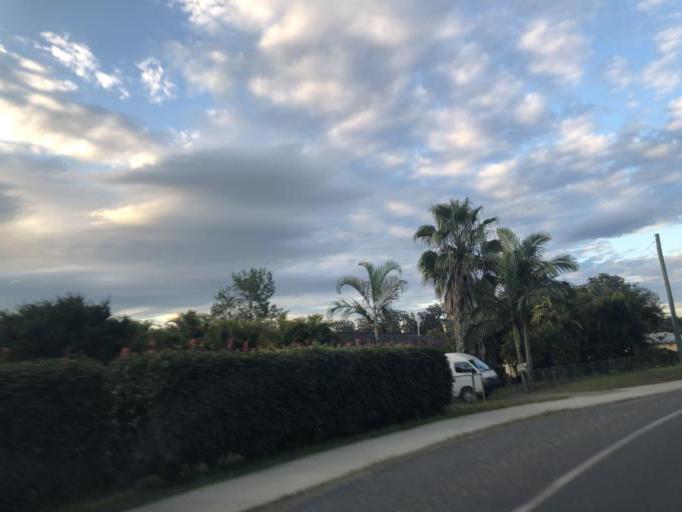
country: AU
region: New South Wales
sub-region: Nambucca Shire
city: Macksville
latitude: -30.7303
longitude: 152.9141
